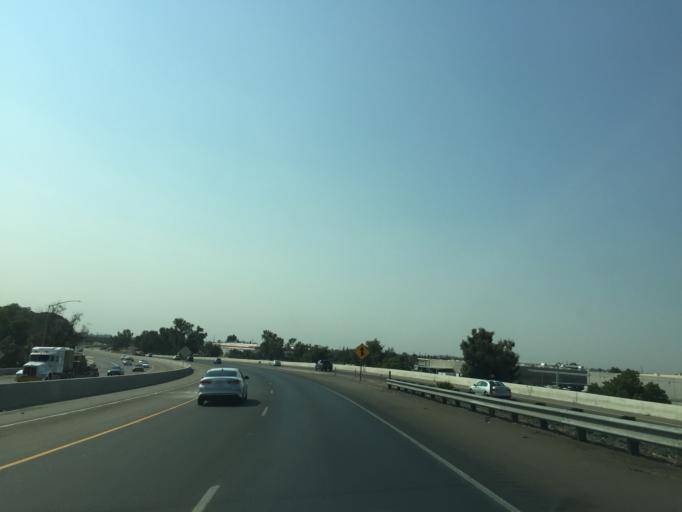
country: US
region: California
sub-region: Merced County
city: Merced
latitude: 37.3124
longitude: -120.5144
